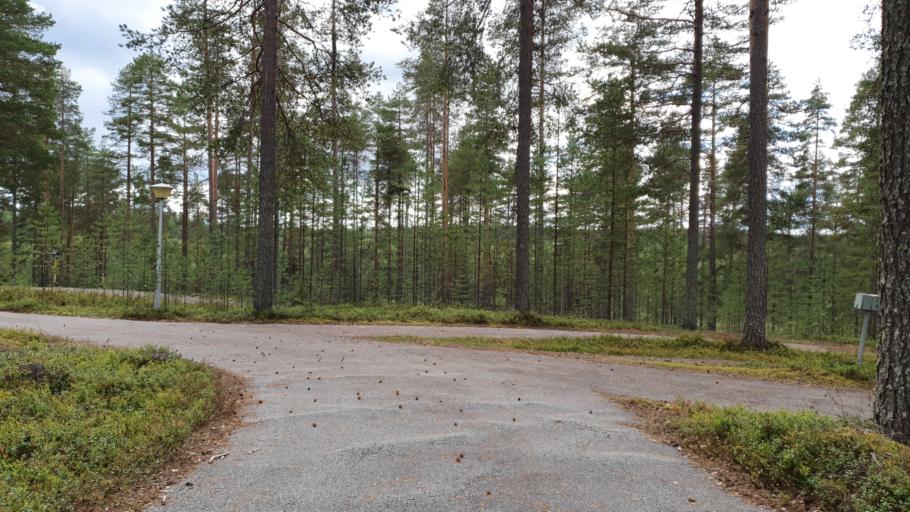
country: FI
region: Kainuu
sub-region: Kehys-Kainuu
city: Kuhmo
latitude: 64.1158
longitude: 29.5885
